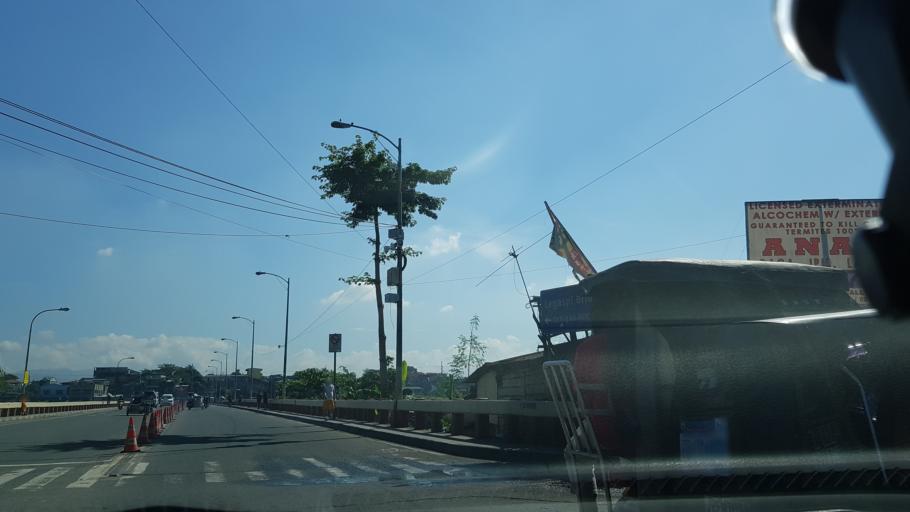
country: PH
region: Calabarzon
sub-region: Province of Rizal
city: Cainta
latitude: 14.5757
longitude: 121.0987
